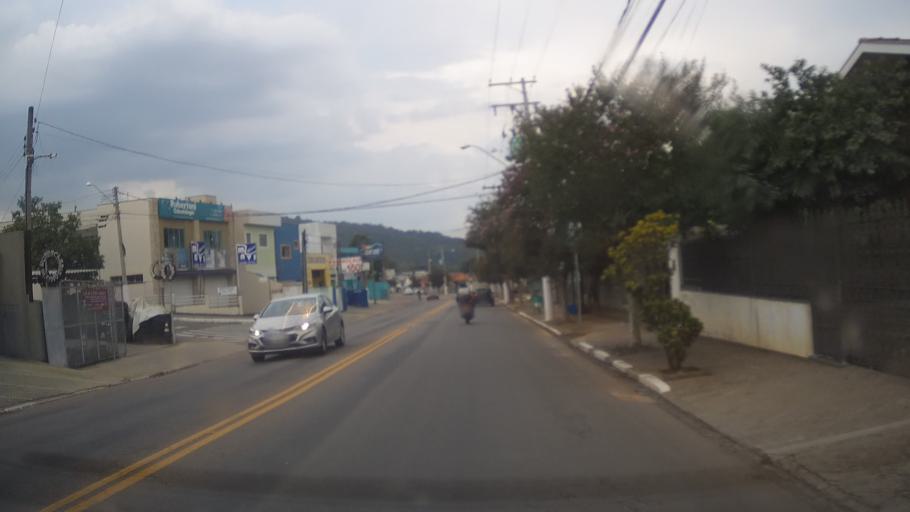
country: BR
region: Sao Paulo
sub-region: Itupeva
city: Itupeva
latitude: -23.1626
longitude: -47.0552
